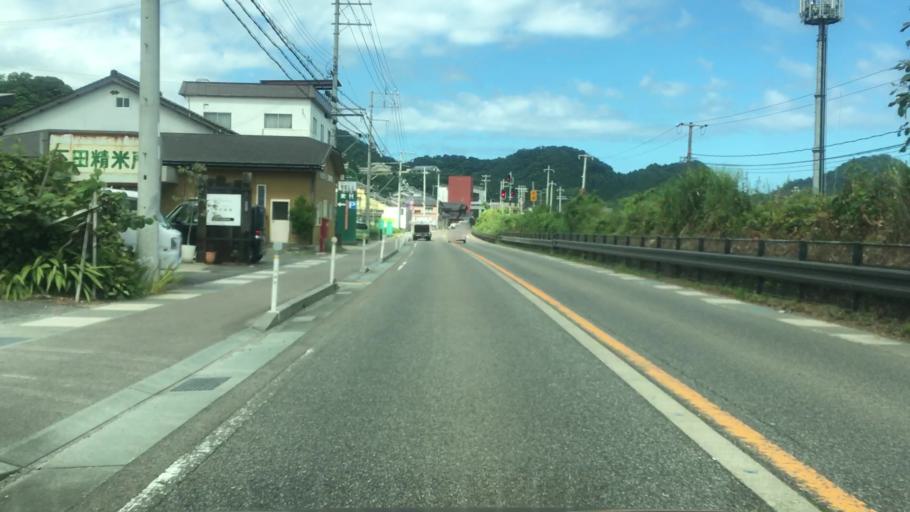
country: JP
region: Tottori
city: Tottori
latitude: 35.6191
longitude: 134.4596
